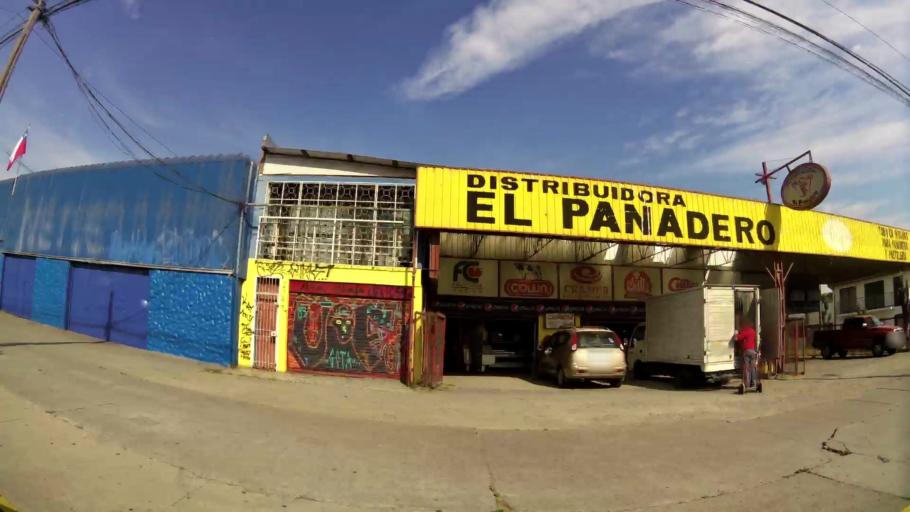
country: CL
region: Santiago Metropolitan
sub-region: Provincia de Santiago
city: La Pintana
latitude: -33.5271
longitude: -70.6358
